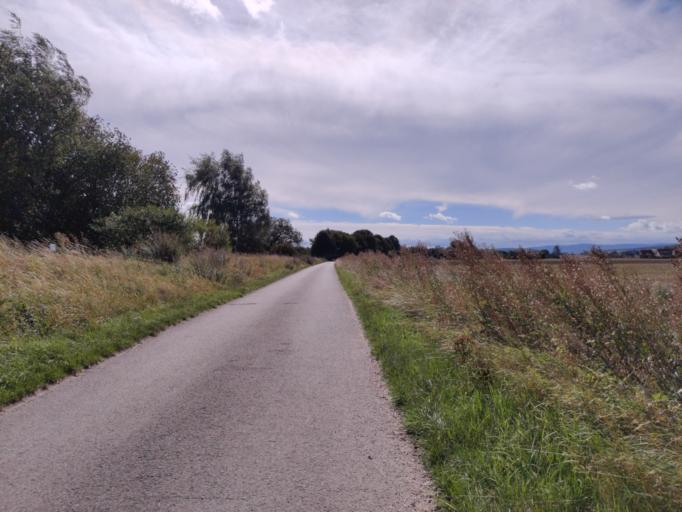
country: DE
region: Lower Saxony
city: Heere
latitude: 52.0734
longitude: 10.2526
